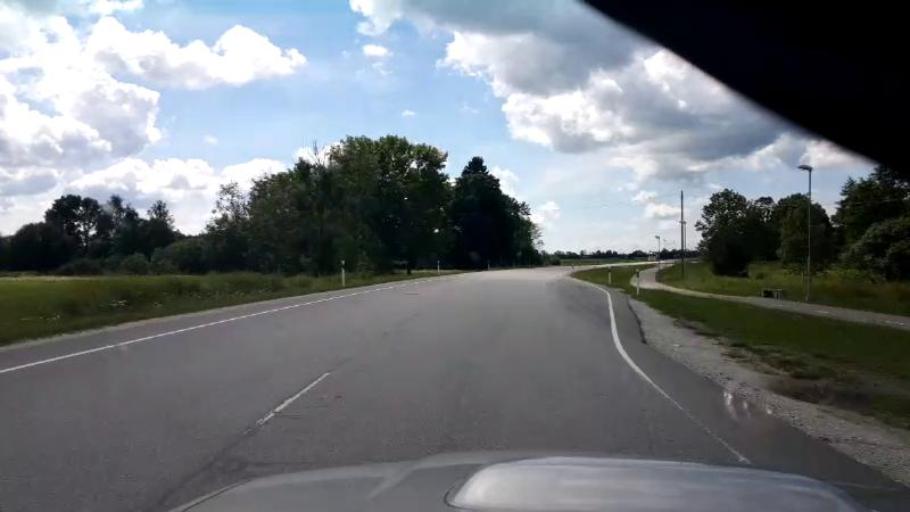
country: EE
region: Jaervamaa
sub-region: Jaerva-Jaani vald
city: Jarva-Jaani
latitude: 59.0228
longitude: 25.7054
